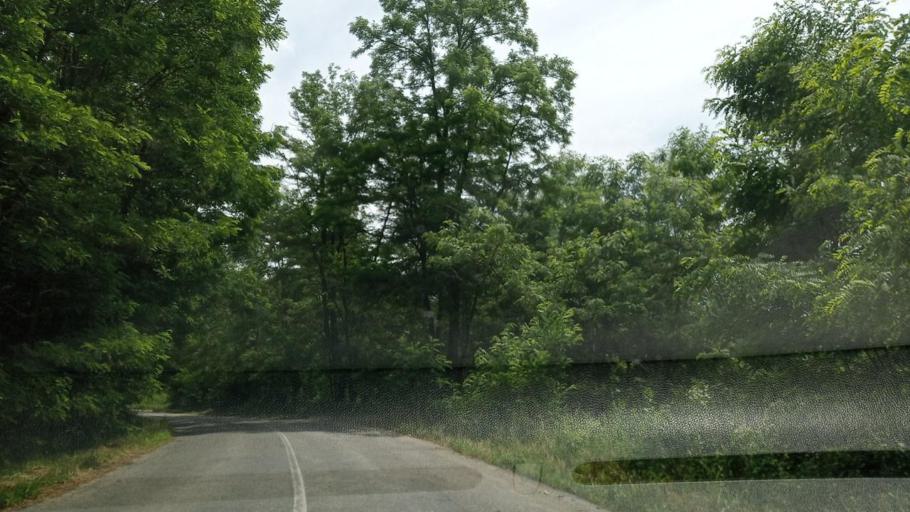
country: RO
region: Sibiu
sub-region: Comuna Porumbacu de Jos
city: Porumbacu de Jos
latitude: 45.7336
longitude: 24.4679
